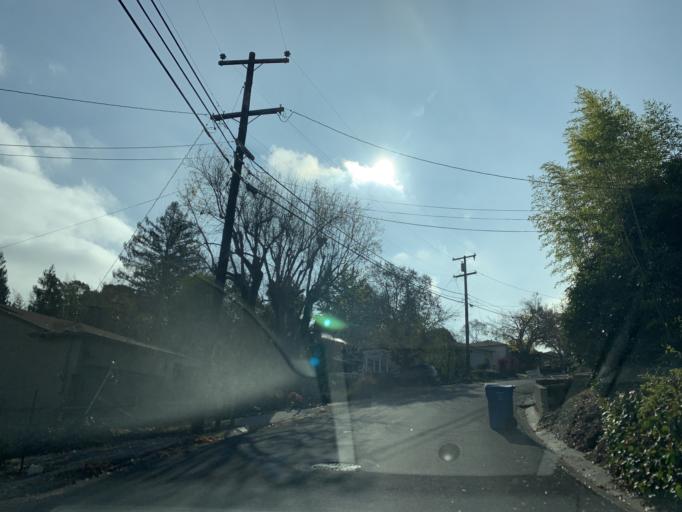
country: US
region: California
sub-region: Contra Costa County
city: Saranap
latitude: 37.8861
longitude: -122.0669
